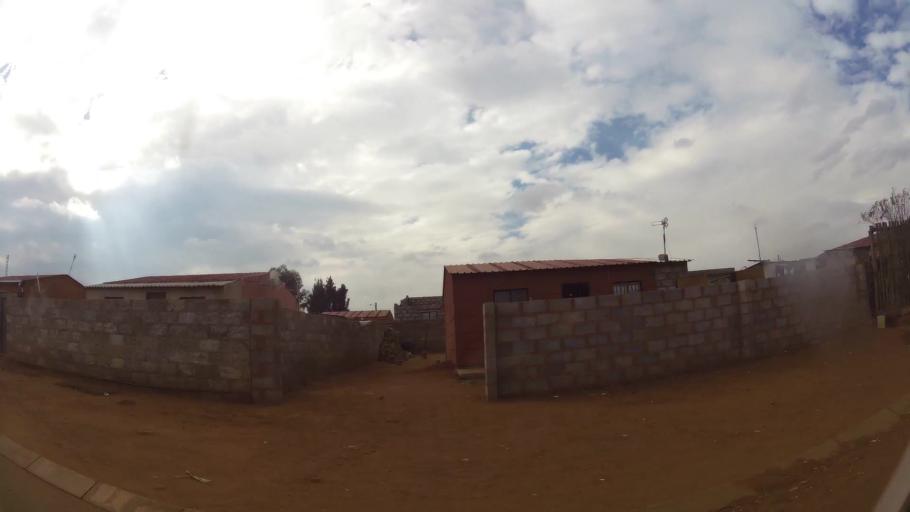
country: ZA
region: Gauteng
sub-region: Ekurhuleni Metropolitan Municipality
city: Germiston
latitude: -26.4007
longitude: 28.1499
